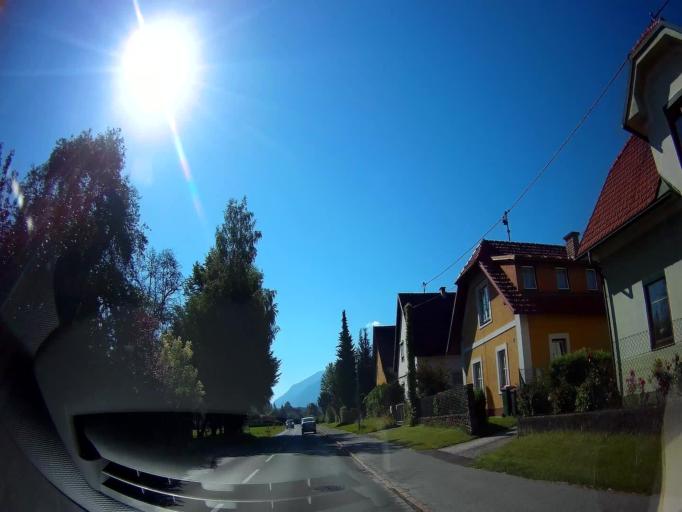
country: AT
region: Carinthia
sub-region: Politischer Bezirk Volkermarkt
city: Eberndorf
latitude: 46.5901
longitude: 14.6425
